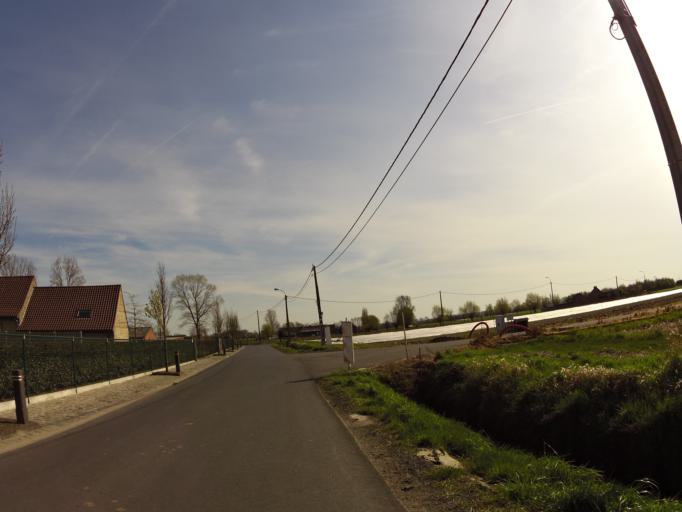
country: BE
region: Flanders
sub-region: Provincie West-Vlaanderen
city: Jabbeke
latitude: 51.1516
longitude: 3.0451
